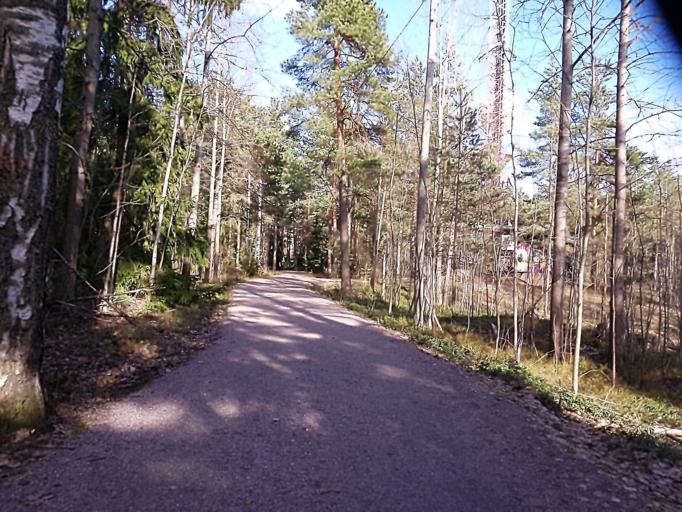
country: FI
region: Uusimaa
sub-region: Helsinki
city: Helsinki
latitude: 60.2195
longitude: 24.9198
